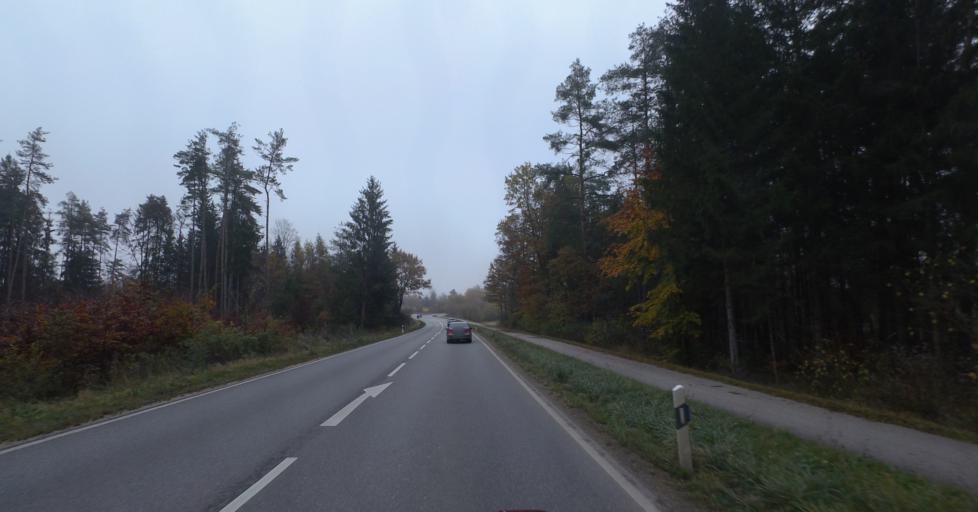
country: DE
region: Bavaria
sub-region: Upper Bavaria
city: Unterneukirchen
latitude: 48.1503
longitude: 12.6105
